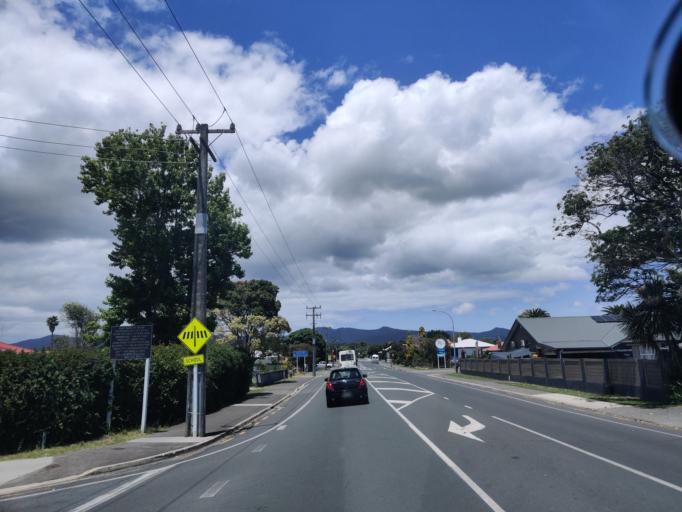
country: NZ
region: Northland
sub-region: Far North District
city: Kaitaia
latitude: -35.1069
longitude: 173.2587
